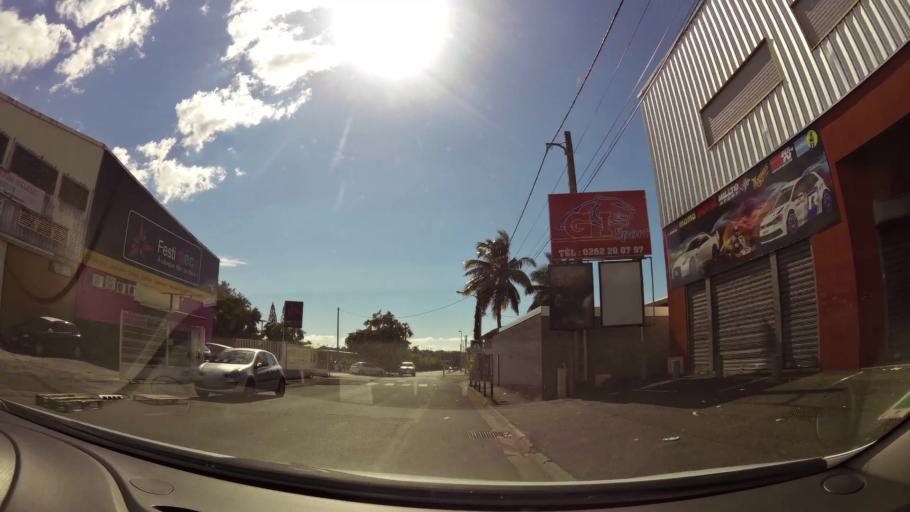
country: RE
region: Reunion
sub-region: Reunion
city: Saint-Denis
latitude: -20.8896
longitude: 55.4962
